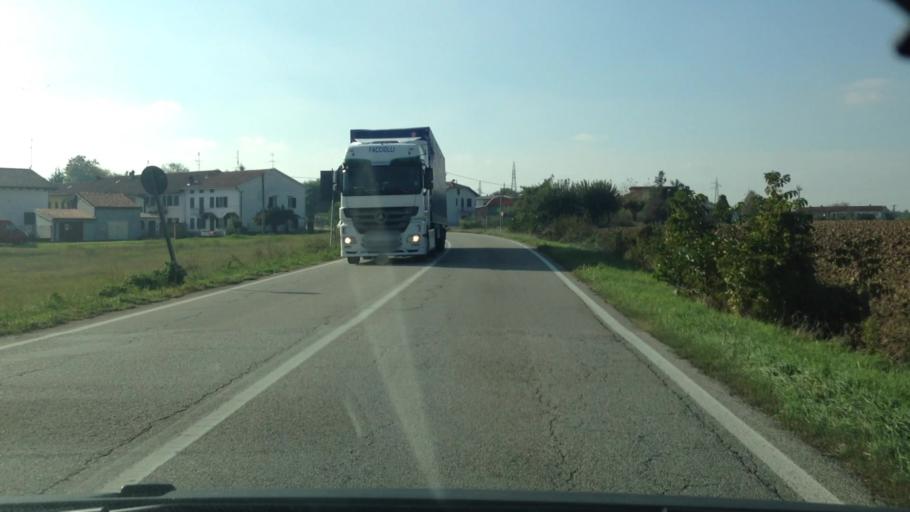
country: IT
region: Piedmont
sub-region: Provincia di Alessandria
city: Felizzano
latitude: 44.9010
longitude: 8.4371
